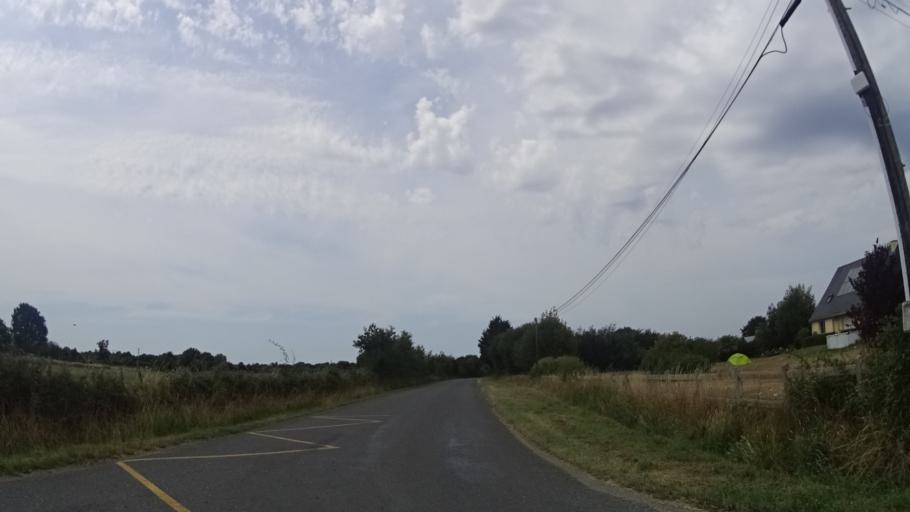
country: FR
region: Pays de la Loire
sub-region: Departement de la Loire-Atlantique
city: Fay-de-Bretagne
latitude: 47.4169
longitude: -1.7757
